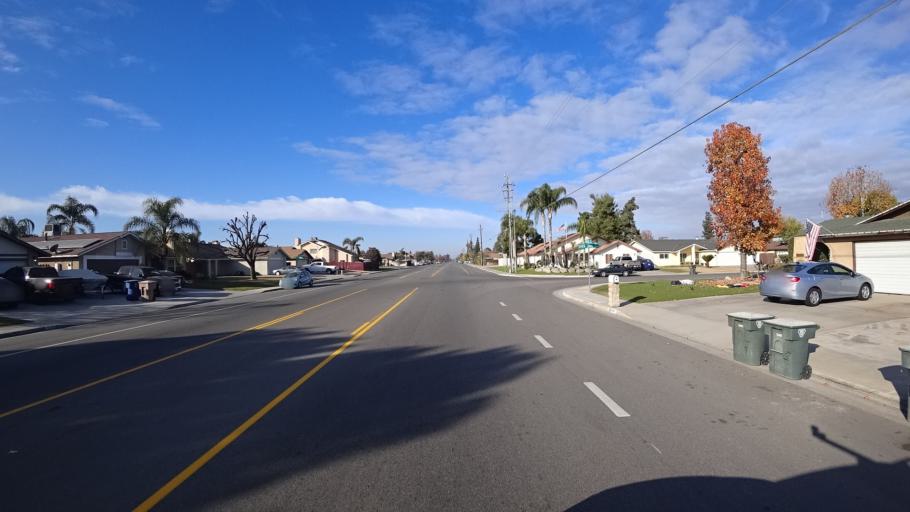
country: US
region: California
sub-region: Kern County
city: Greenfield
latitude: 35.3032
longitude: -119.0410
